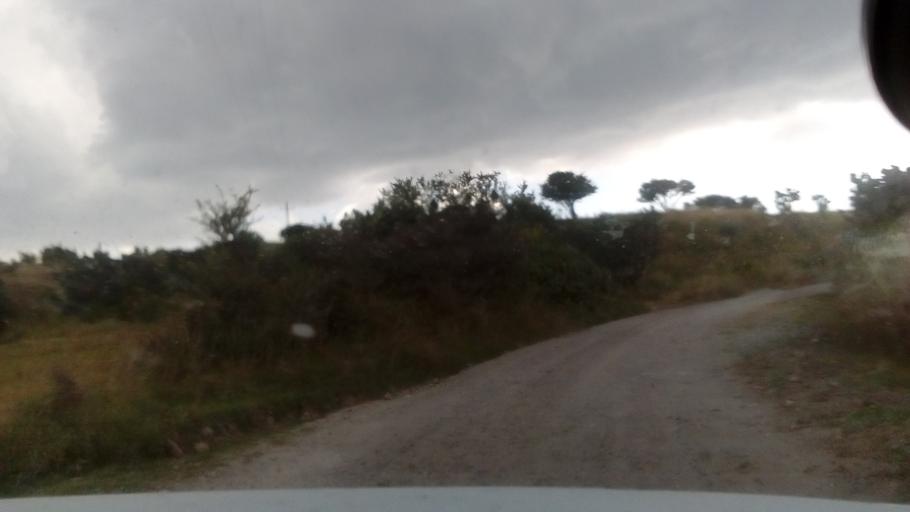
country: MX
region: Guanajuato
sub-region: Silao de la Victoria
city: San Francisco (Banos de Agua Caliente)
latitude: 21.1963
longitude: -101.4217
